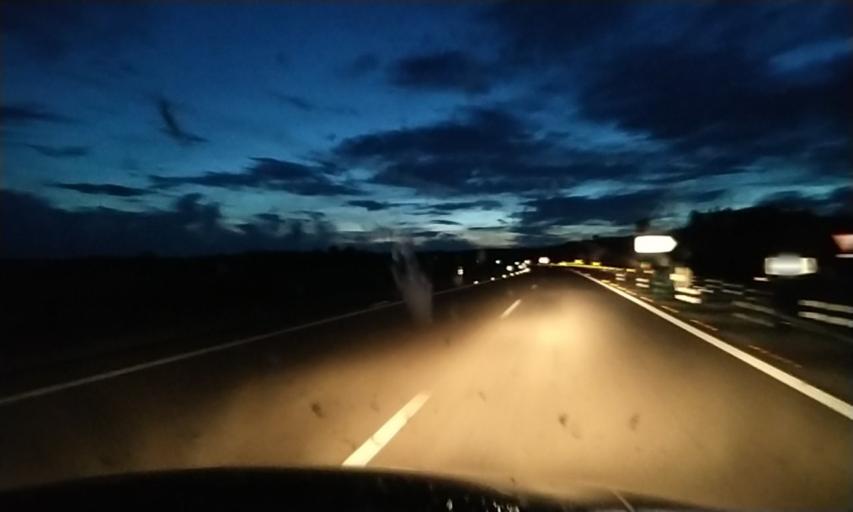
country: ES
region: Extremadura
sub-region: Provincia de Caceres
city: Galisteo
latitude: 39.9851
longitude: -6.2673
